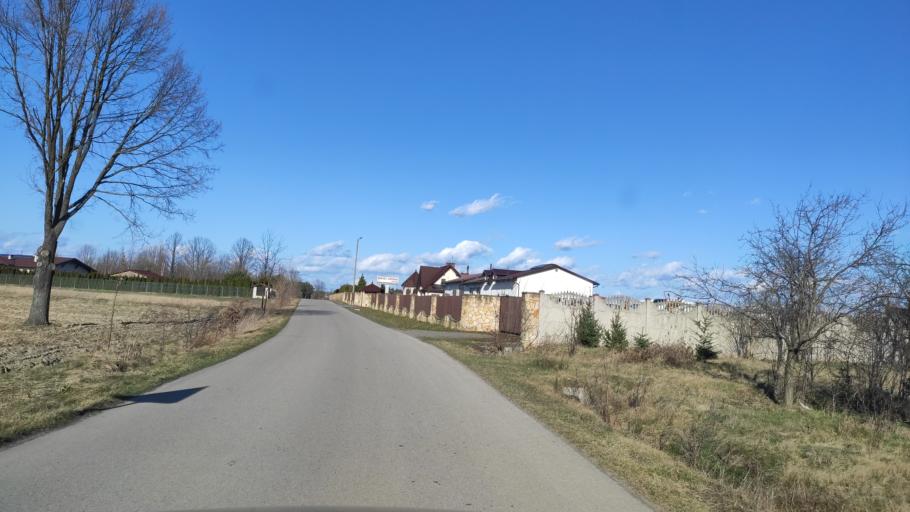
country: PL
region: Masovian Voivodeship
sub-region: Powiat radomski
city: Jastrzebia
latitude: 51.4544
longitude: 21.2572
